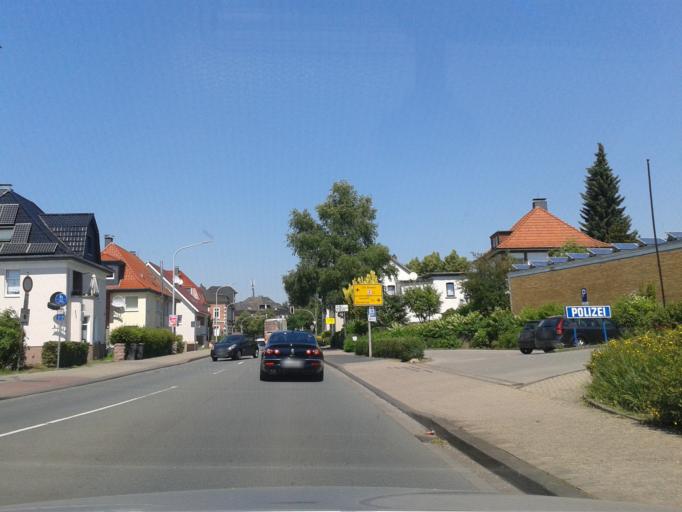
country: DE
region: North Rhine-Westphalia
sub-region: Regierungsbezirk Detmold
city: Lemgo
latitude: 52.0250
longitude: 8.9134
